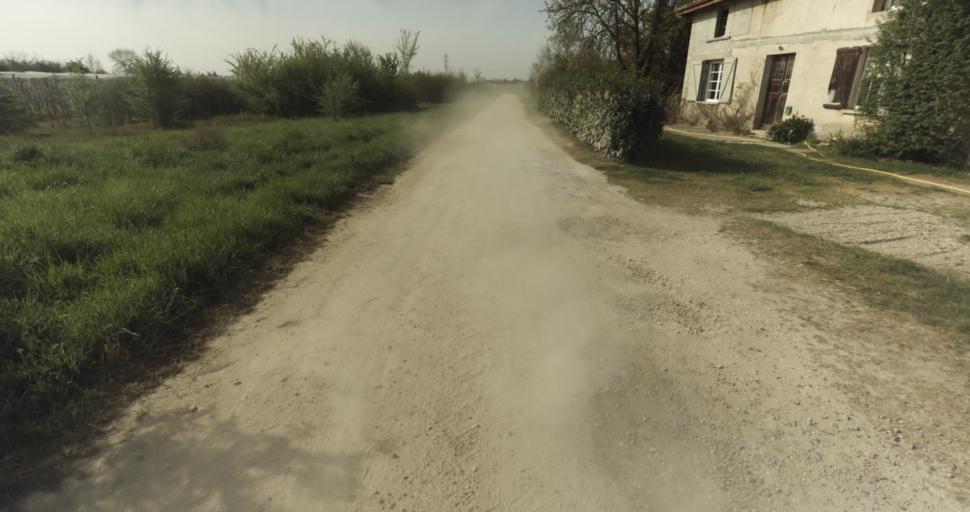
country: FR
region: Midi-Pyrenees
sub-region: Departement du Tarn-et-Garonne
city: Moissac
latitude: 44.1123
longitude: 1.1318
